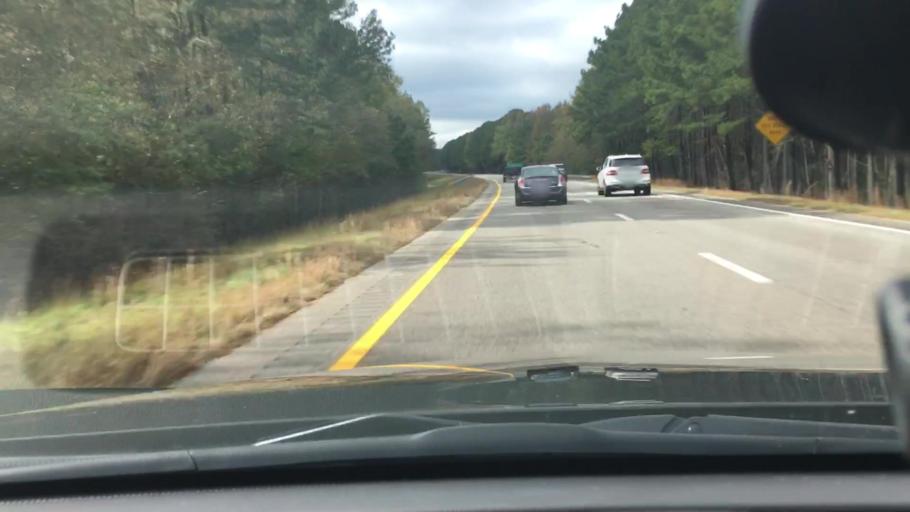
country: US
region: North Carolina
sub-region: Wake County
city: Zebulon
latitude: 35.7981
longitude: -78.1740
